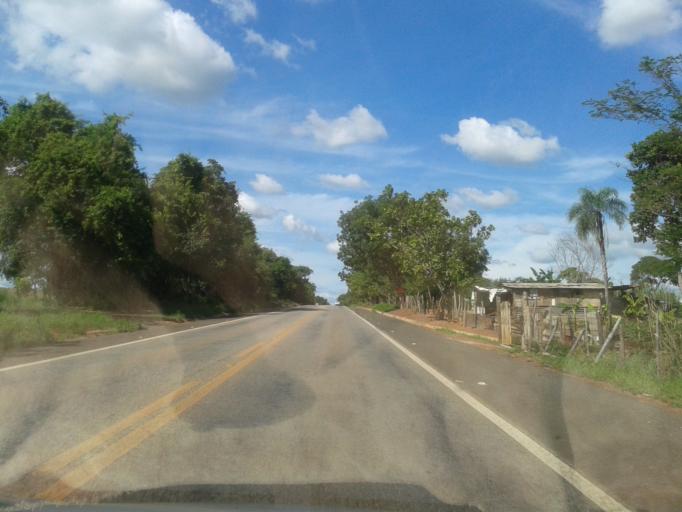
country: BR
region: Goias
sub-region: Mozarlandia
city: Mozarlandia
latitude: -15.0676
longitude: -50.6168
